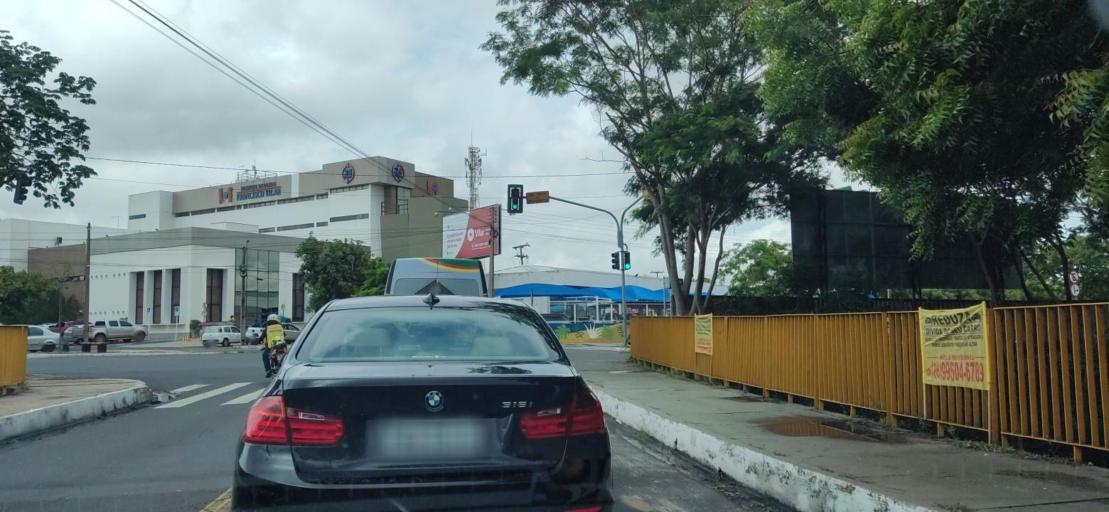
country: BR
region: Piaui
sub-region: Teresina
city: Teresina
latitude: -5.0812
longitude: -42.8077
